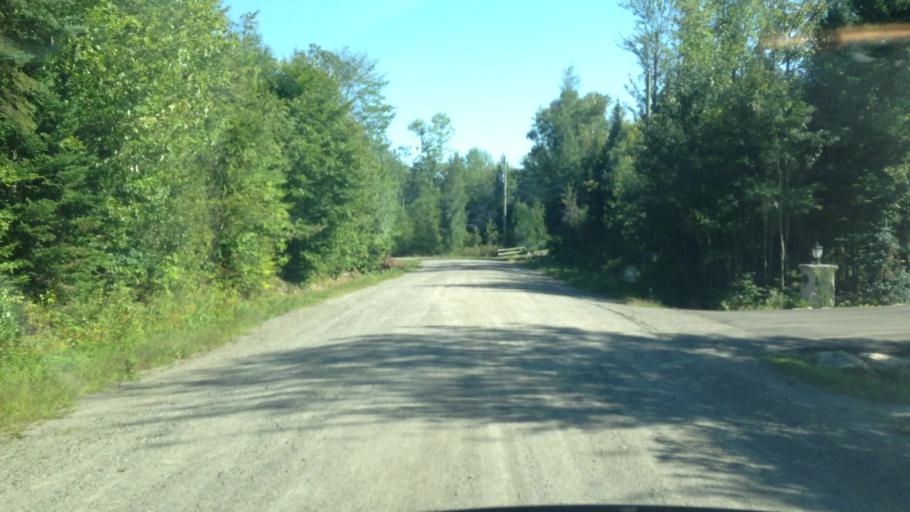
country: CA
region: Quebec
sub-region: Laurentides
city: Prevost
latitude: 45.8523
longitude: -74.0320
